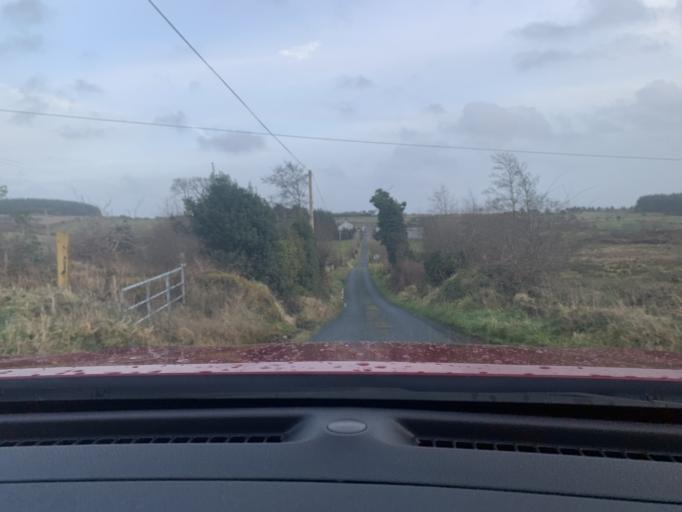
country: IE
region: Connaught
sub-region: Roscommon
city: Ballaghaderreen
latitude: 53.9507
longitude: -8.5191
